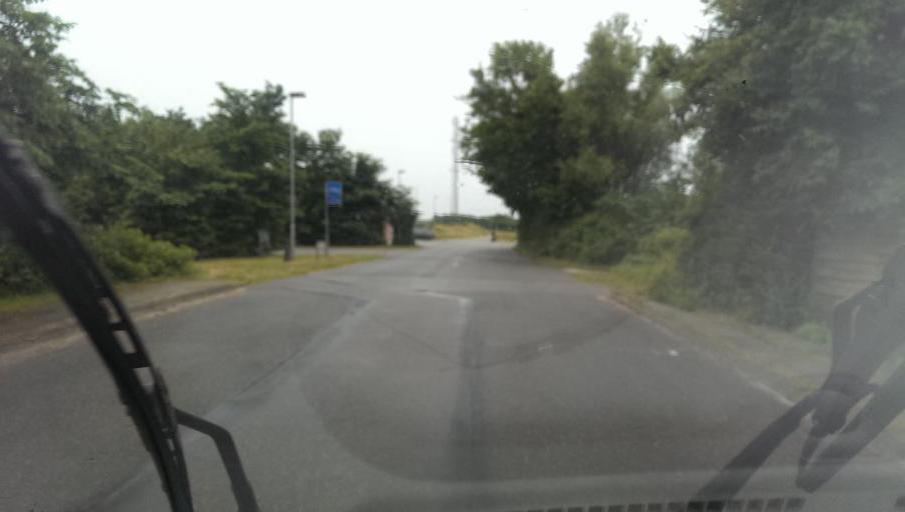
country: DK
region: South Denmark
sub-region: Varde Kommune
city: Oksbol
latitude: 55.7791
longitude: 8.2834
